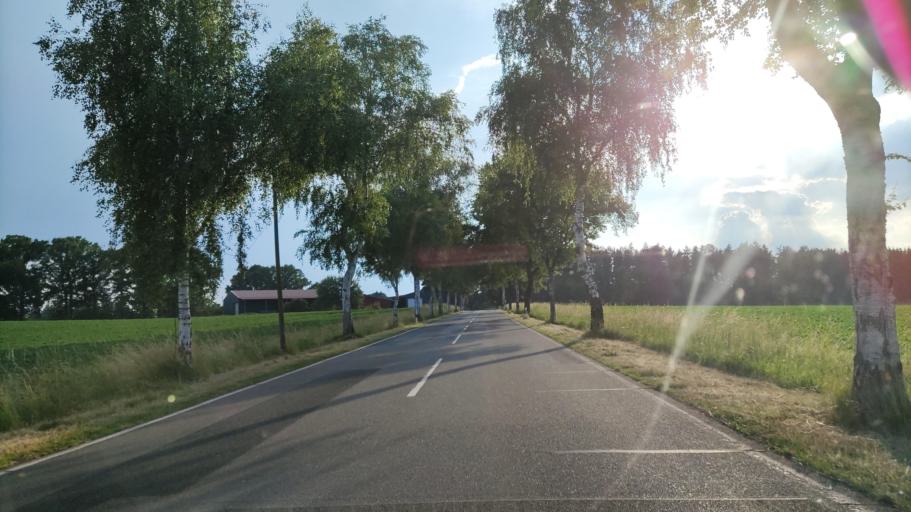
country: DE
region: Lower Saxony
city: Egestorf
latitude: 53.1522
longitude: 10.0769
